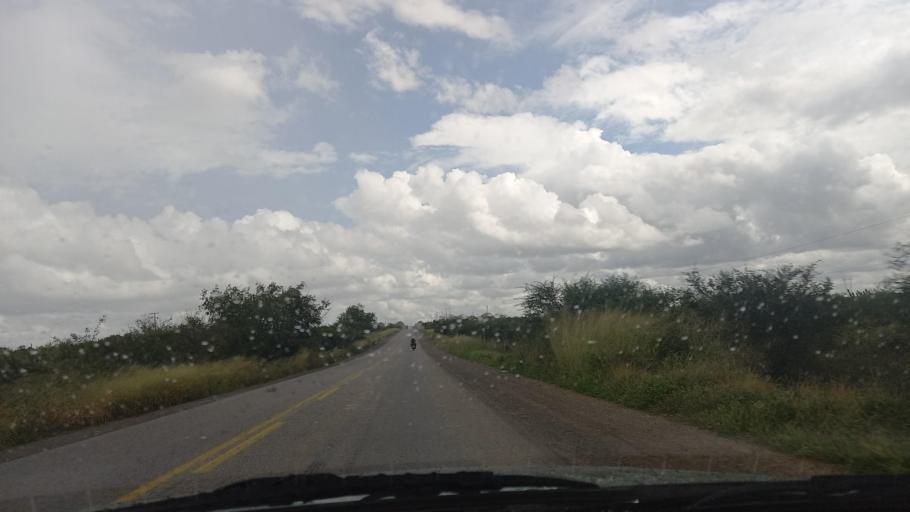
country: BR
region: Pernambuco
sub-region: Cachoeirinha
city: Cachoeirinha
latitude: -8.5626
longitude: -36.2773
